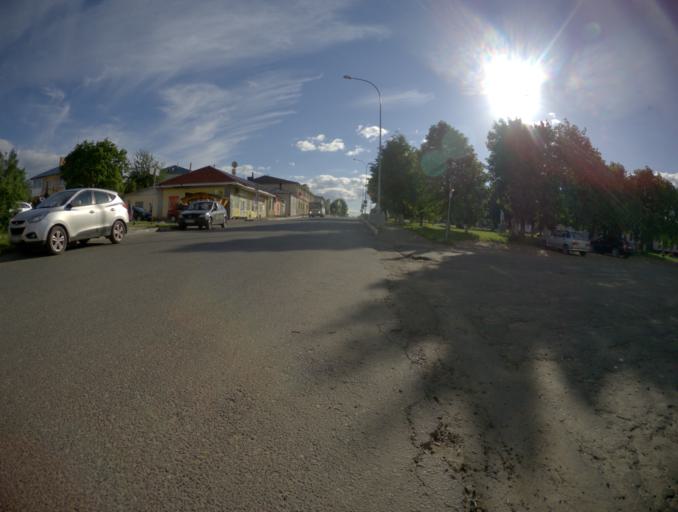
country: RU
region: Ivanovo
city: Lezhnevo
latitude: 56.7756
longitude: 40.8884
